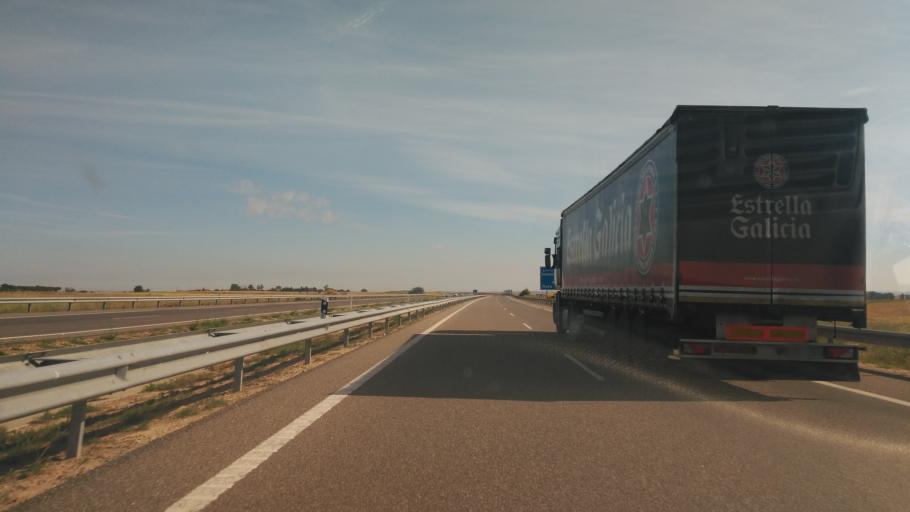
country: ES
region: Castille and Leon
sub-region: Provincia de Zamora
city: Morales del Vino
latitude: 41.4334
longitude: -5.7210
